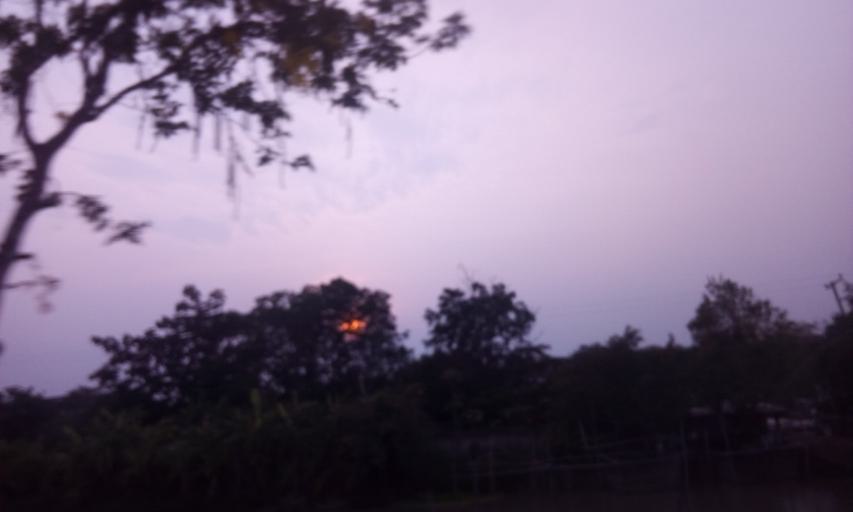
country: TH
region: Bangkok
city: Nong Chok
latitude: 13.9565
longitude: 100.8951
